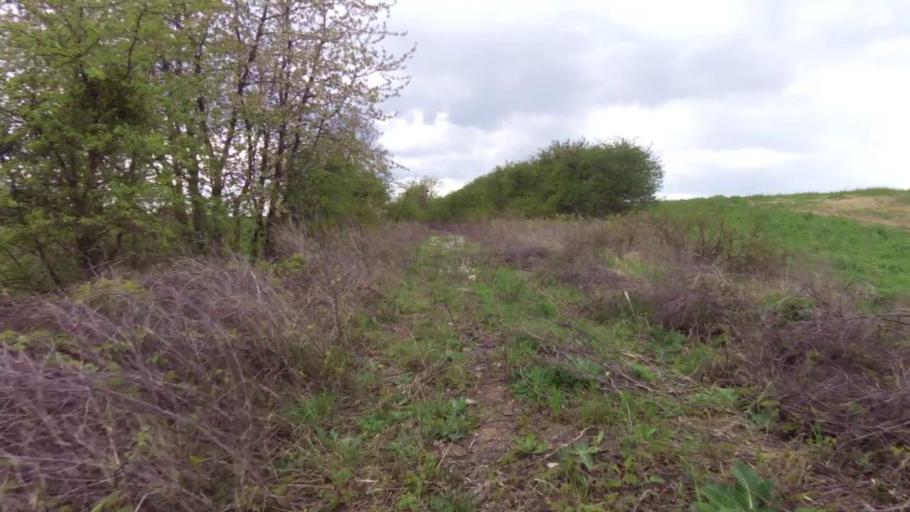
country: PL
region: West Pomeranian Voivodeship
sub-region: Powiat choszczenski
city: Pelczyce
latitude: 53.0462
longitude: 15.2947
